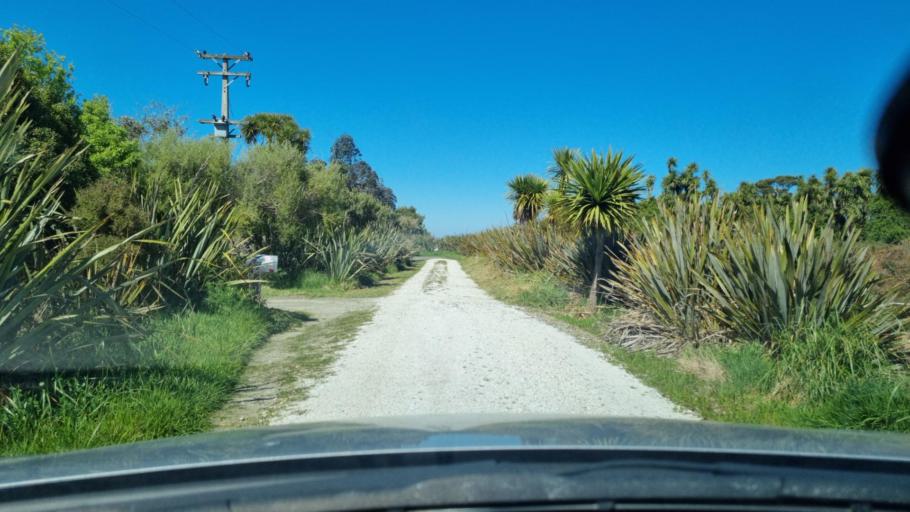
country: NZ
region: Southland
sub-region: Invercargill City
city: Invercargill
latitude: -46.4526
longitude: 168.3166
